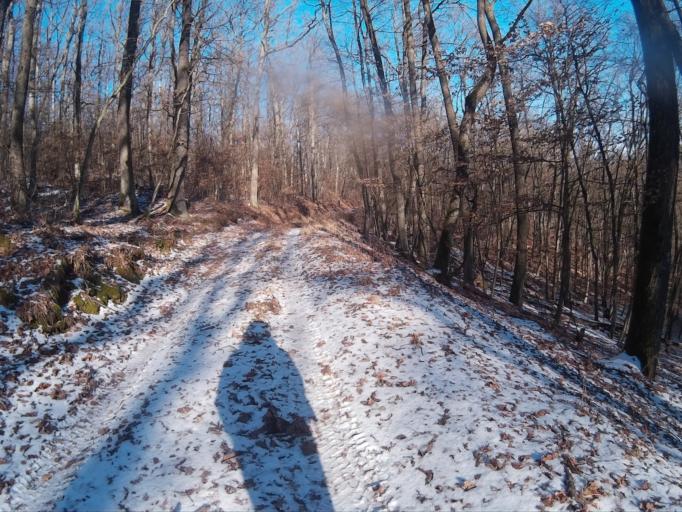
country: HU
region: Borsod-Abauj-Zemplen
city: Rudabanya
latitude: 48.4958
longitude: 20.5863
